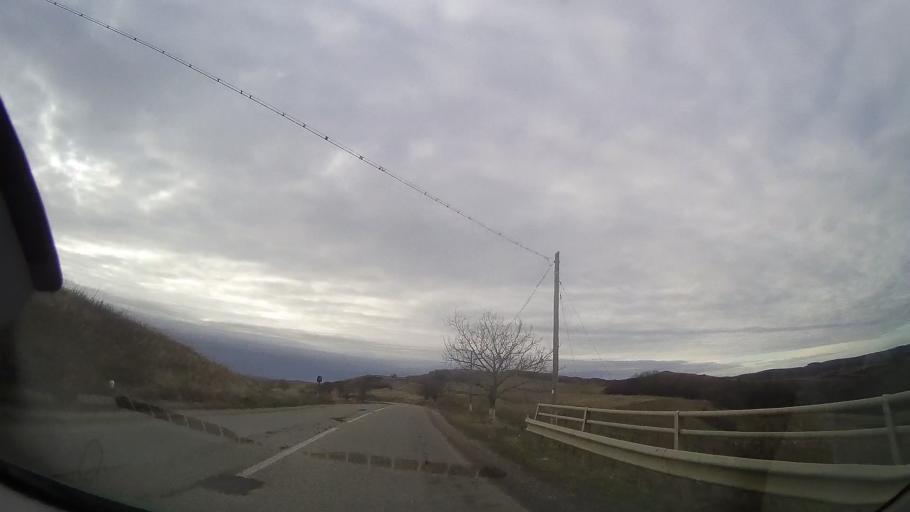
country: RO
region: Bistrita-Nasaud
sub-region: Comuna Budesti
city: Budesti
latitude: 46.8909
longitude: 24.2433
